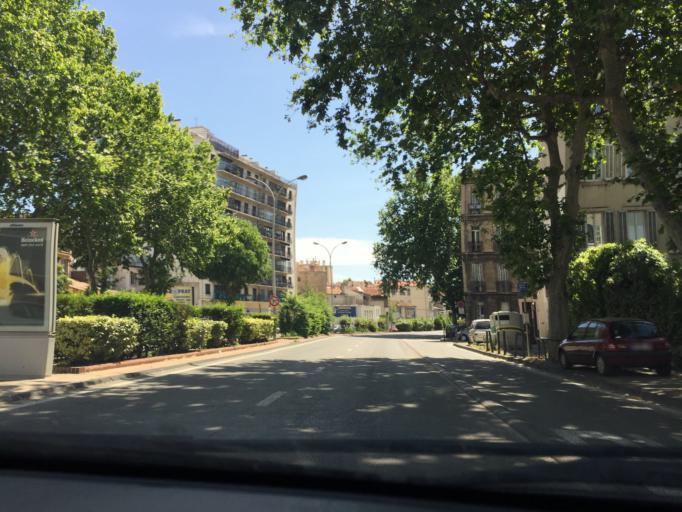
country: FR
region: Provence-Alpes-Cote d'Azur
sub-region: Departement des Bouches-du-Rhone
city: Marseille 04
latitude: 43.3095
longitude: 5.4029
